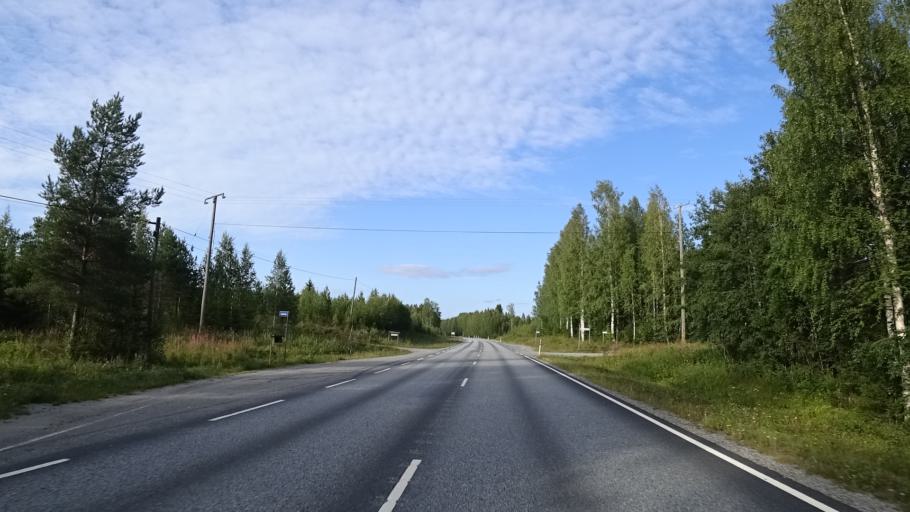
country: FI
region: North Karelia
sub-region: Joensuu
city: Eno
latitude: 62.8176
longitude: 30.1853
